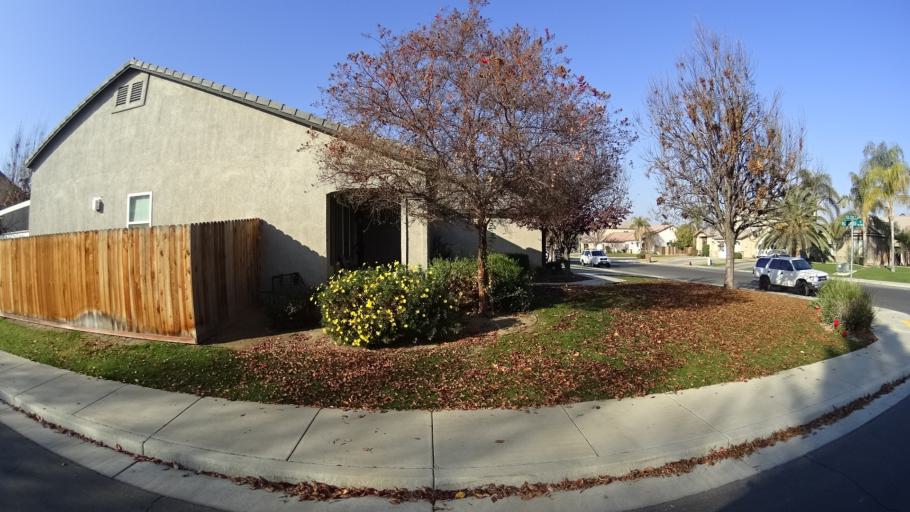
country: US
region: California
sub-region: Kern County
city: Greenacres
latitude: 35.3046
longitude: -119.1221
